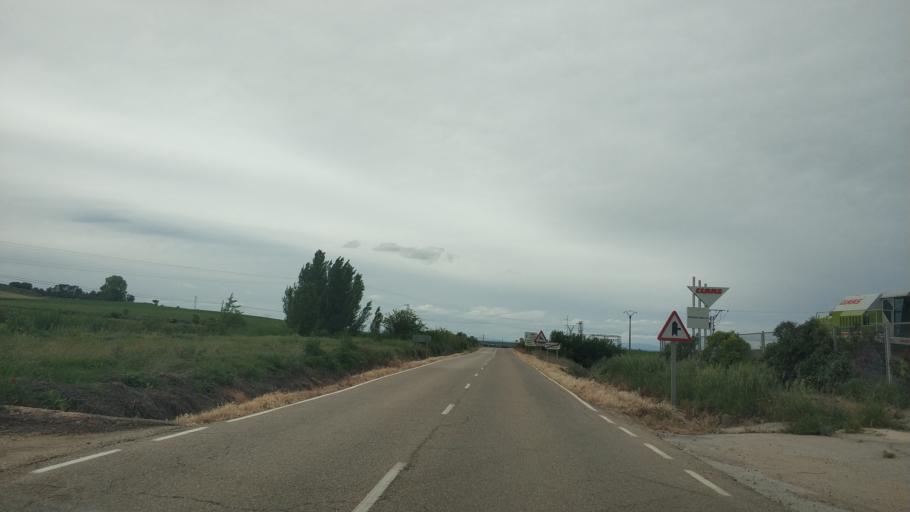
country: ES
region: Castille and Leon
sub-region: Provincia de Soria
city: Berlanga de Duero
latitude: 41.4721
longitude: -2.8614
